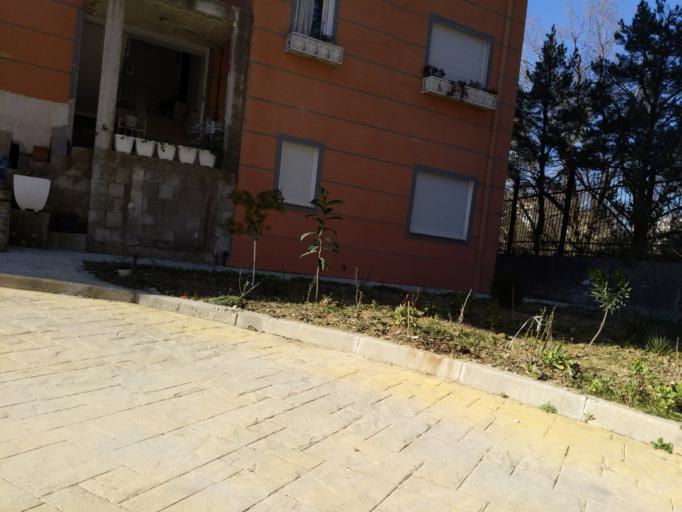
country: AL
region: Tirane
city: Tirana
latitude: 41.3087
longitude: 19.8047
